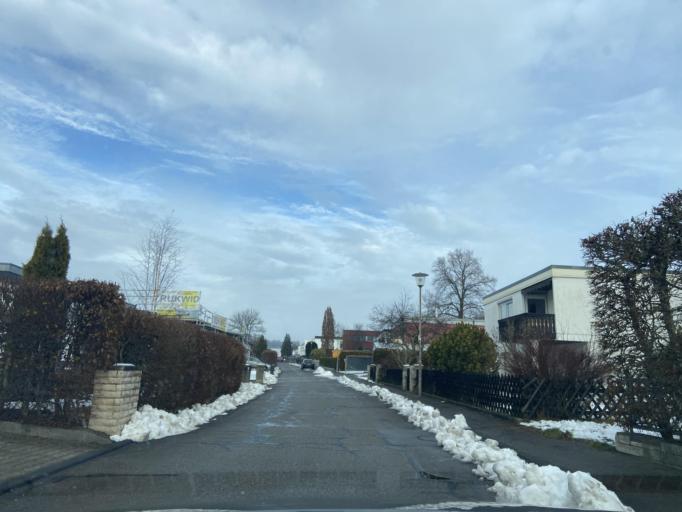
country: DE
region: Baden-Wuerttemberg
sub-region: Tuebingen Region
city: Gammertingen
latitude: 48.2513
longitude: 9.2256
